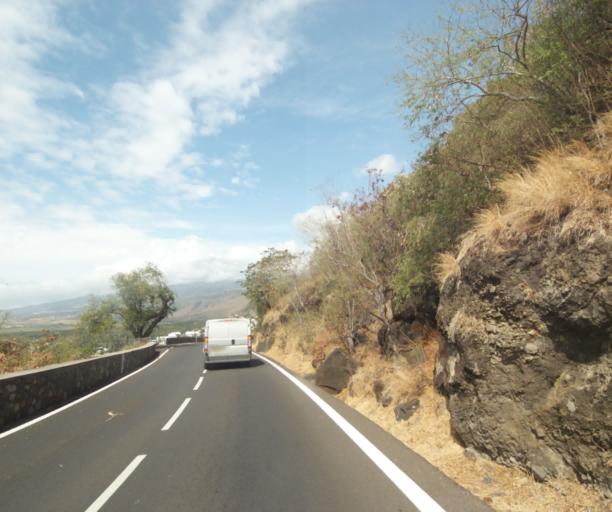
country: RE
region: Reunion
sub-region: Reunion
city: Saint-Paul
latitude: -21.0160
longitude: 55.2702
